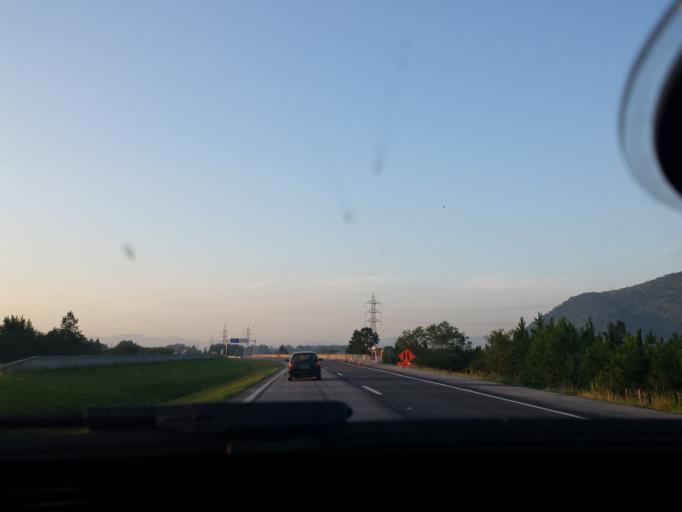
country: BR
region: Santa Catarina
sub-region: Florianopolis
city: Pantano do Sul
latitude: -27.8614
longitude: -48.6453
